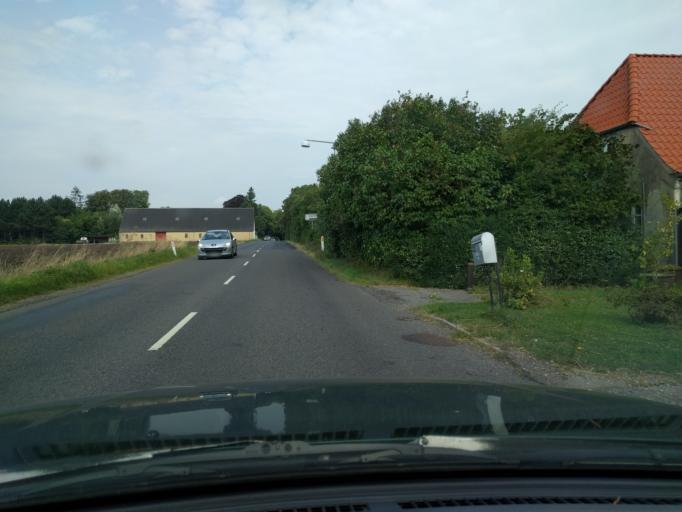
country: DK
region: South Denmark
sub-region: Odense Kommune
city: Bullerup
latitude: 55.3950
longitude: 10.4626
